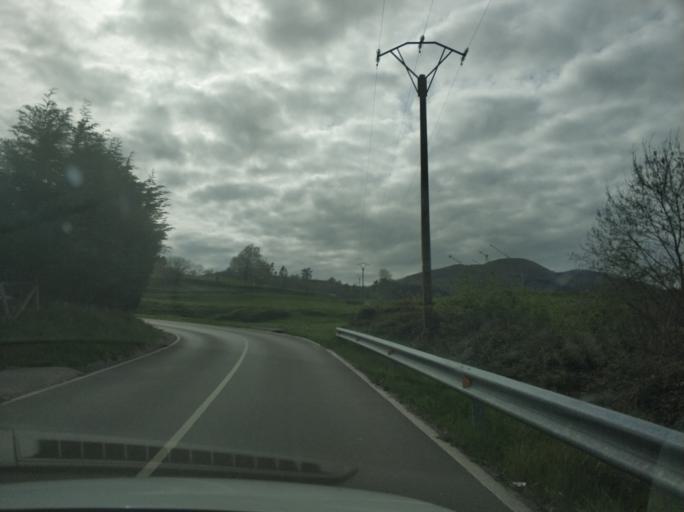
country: ES
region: Cantabria
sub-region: Provincia de Cantabria
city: Ruente
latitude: 43.2382
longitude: -4.2832
